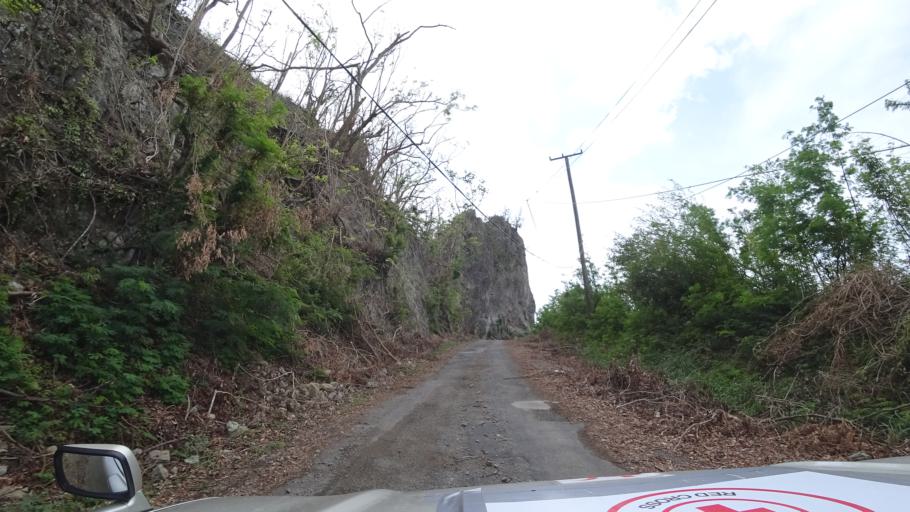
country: DM
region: Saint Mark
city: Soufriere
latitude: 15.2433
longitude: -61.3721
